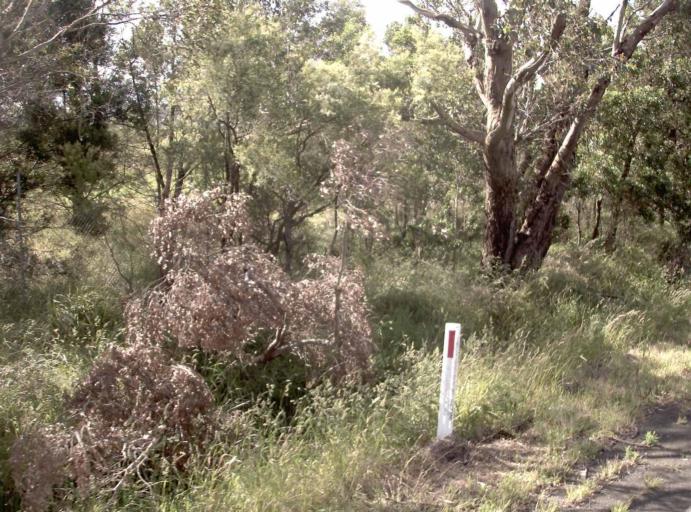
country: AU
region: Victoria
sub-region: Latrobe
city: Morwell
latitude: -38.1737
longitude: 146.4060
